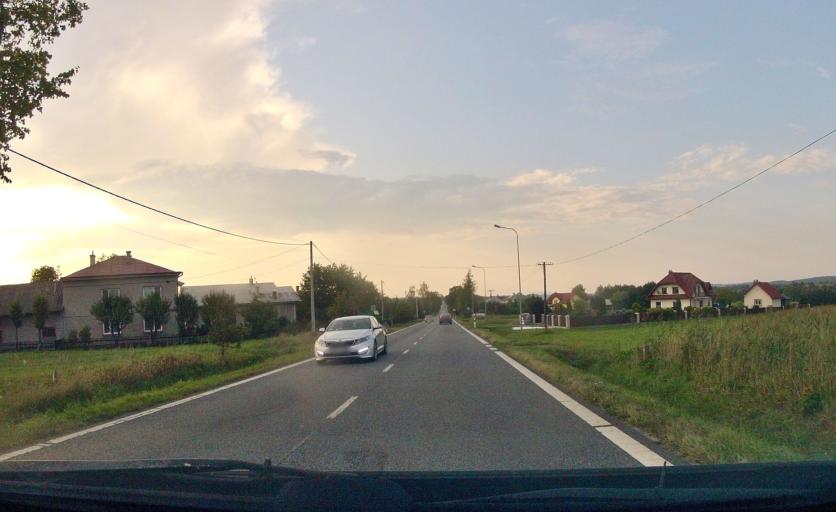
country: PL
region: Subcarpathian Voivodeship
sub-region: Powiat jasielski
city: Nowy Zmigrod
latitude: 49.5937
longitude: 21.5371
